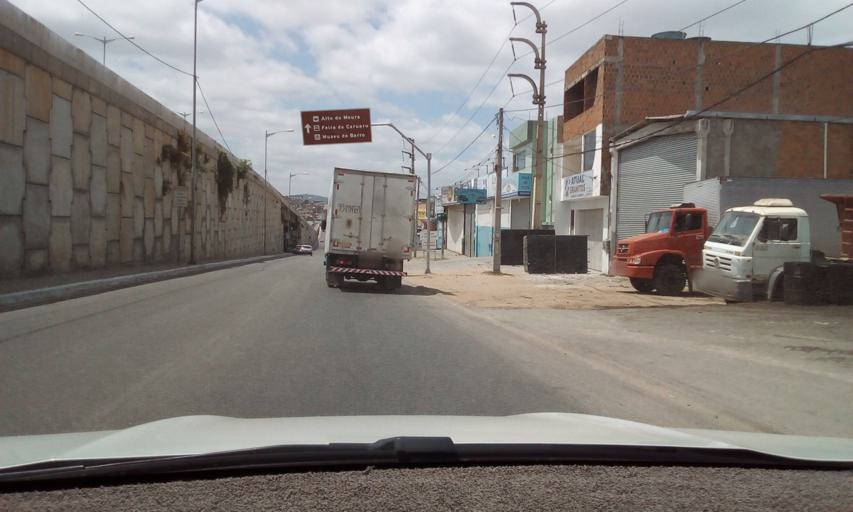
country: BR
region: Pernambuco
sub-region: Caruaru
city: Caruaru
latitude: -8.2746
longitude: -35.9824
